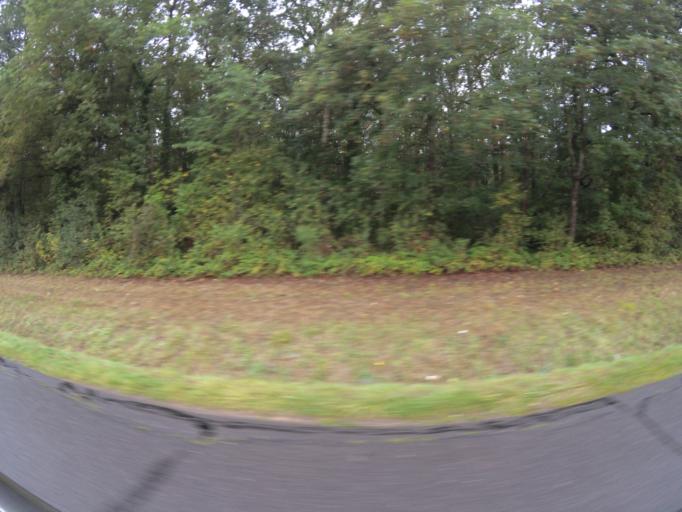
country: FR
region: Ile-de-France
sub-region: Departement de Seine-et-Marne
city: Collegien
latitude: 48.8275
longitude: 2.6876
